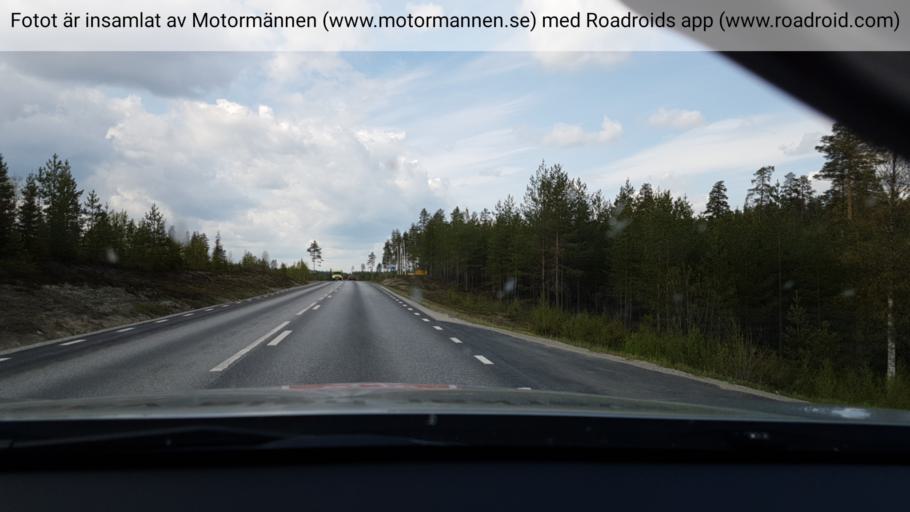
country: SE
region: Vaesterbotten
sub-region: Vindelns Kommun
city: Vindeln
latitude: 64.0573
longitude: 19.6486
